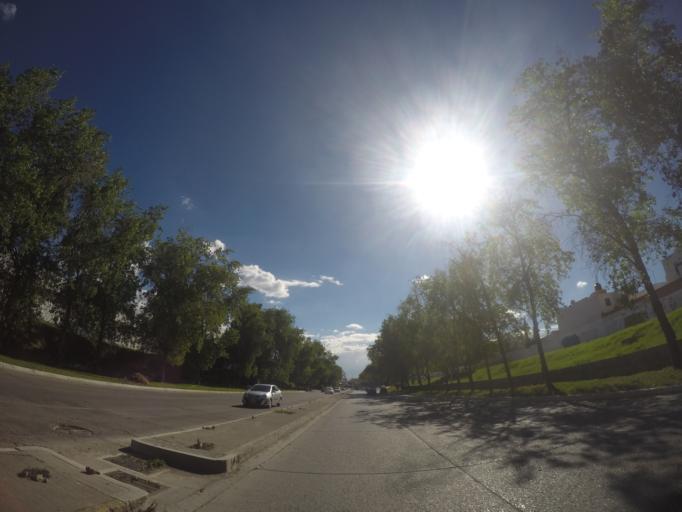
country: MX
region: San Luis Potosi
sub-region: San Luis Potosi
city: San Luis Potosi
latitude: 22.1698
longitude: -100.9771
